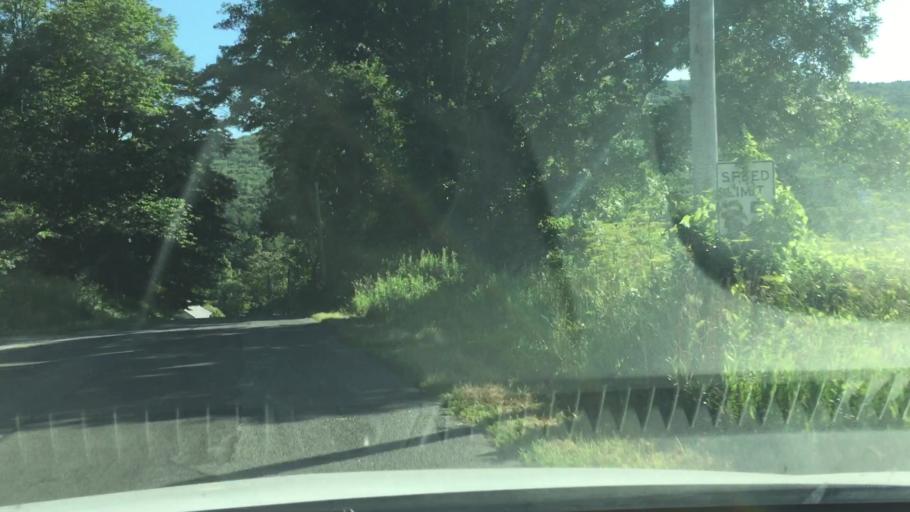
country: US
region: Massachusetts
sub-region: Berkshire County
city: Lee
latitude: 42.2431
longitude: -73.2055
